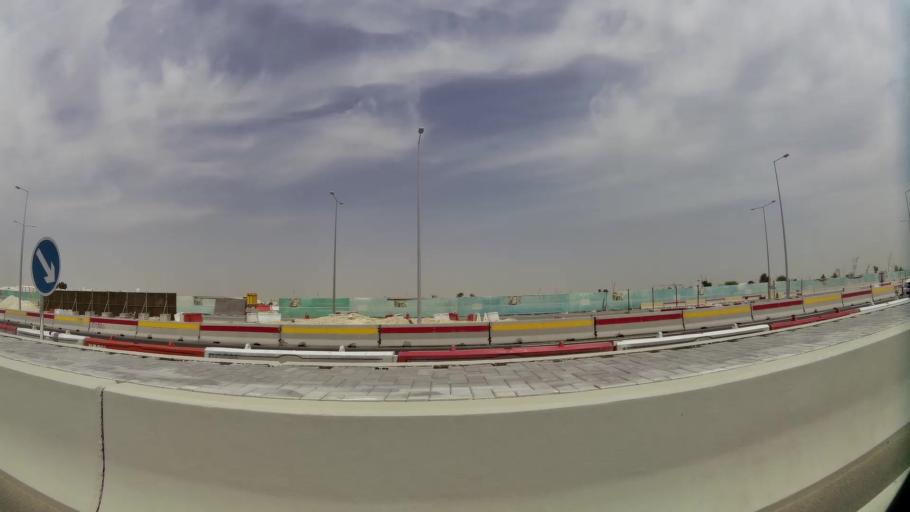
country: QA
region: Baladiyat ar Rayyan
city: Ar Rayyan
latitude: 25.3054
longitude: 51.4149
